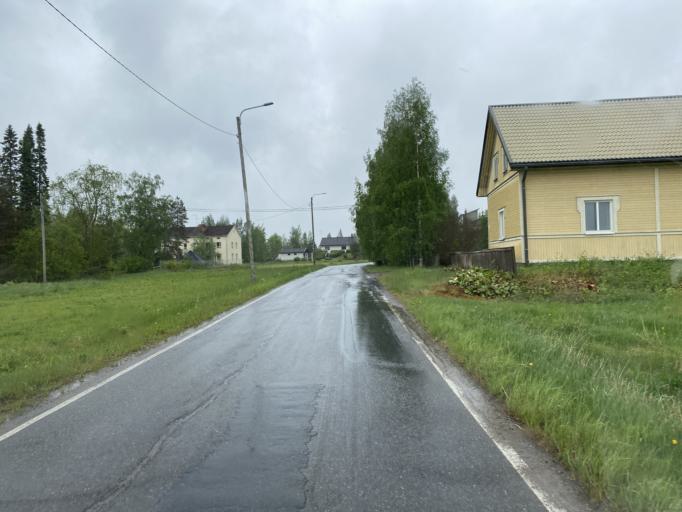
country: FI
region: Haeme
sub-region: Forssa
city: Humppila
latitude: 61.0972
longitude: 23.3164
